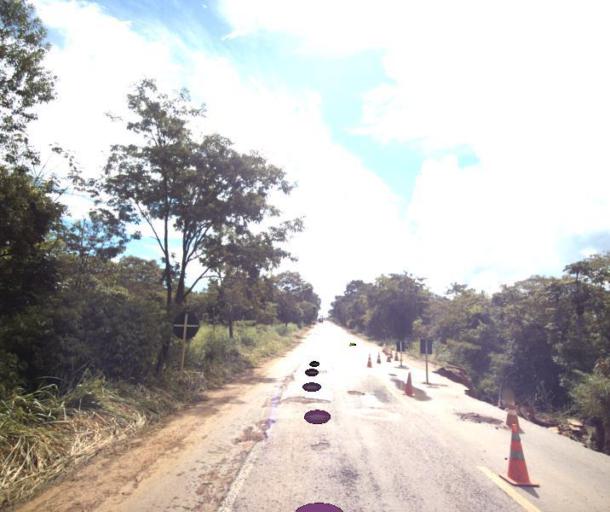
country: BR
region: Goias
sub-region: Petrolina De Goias
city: Petrolina de Goias
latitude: -16.0066
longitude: -49.1305
